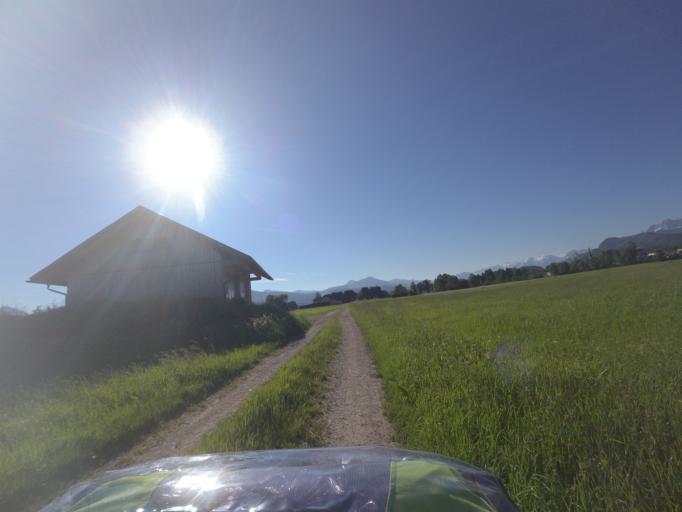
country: AT
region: Salzburg
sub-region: Politischer Bezirk Salzburg-Umgebung
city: Grodig
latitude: 47.7486
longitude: 13.0308
